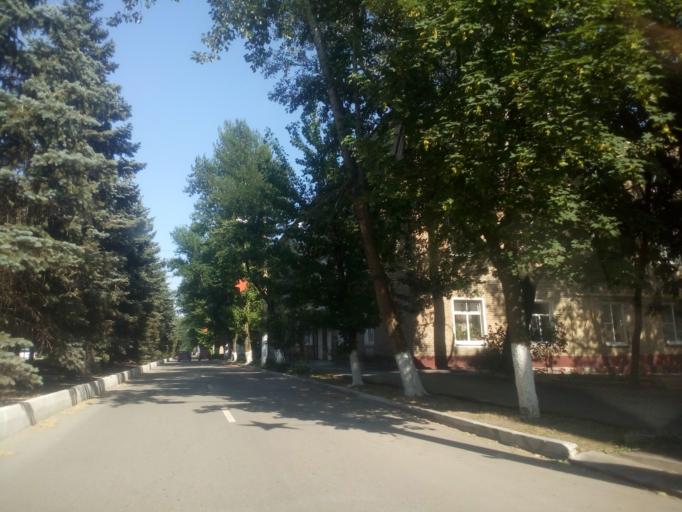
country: RU
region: Rostov
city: Sholokhovskiy
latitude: 48.2820
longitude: 41.0473
